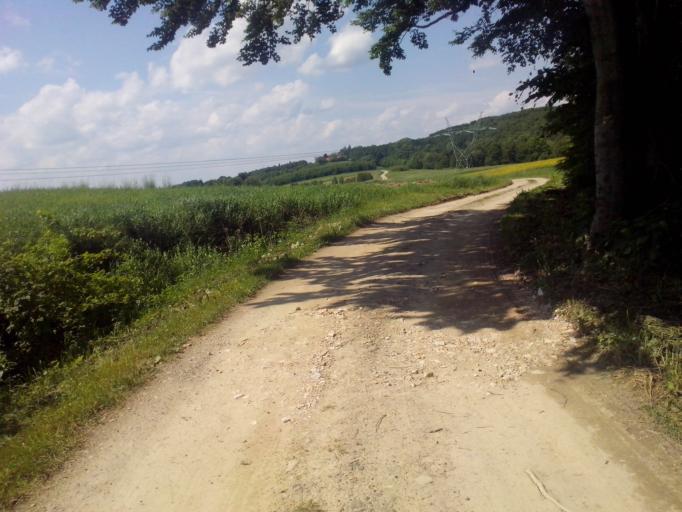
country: PL
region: Subcarpathian Voivodeship
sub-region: Powiat strzyzowski
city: Jawornik
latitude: 49.8422
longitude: 21.8535
